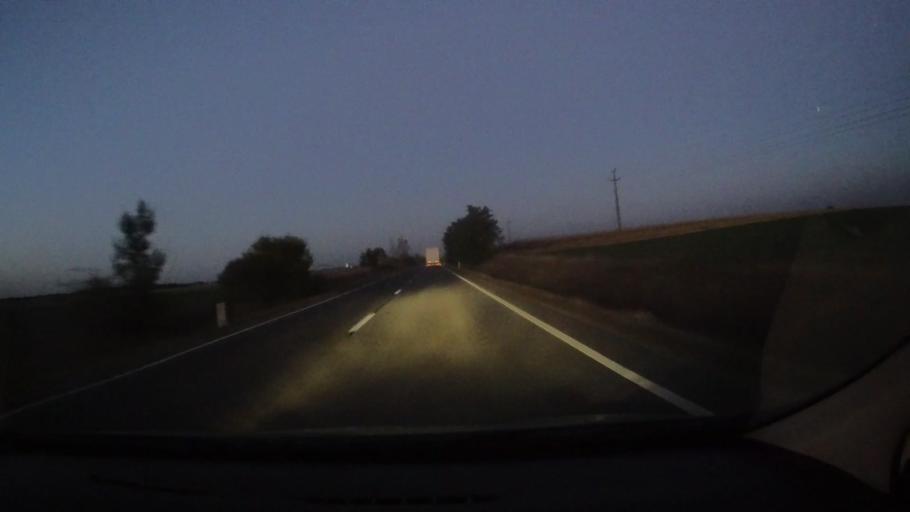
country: RO
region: Bihor
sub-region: Comuna Curtuiuseni
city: Curtuiseni
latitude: 47.5251
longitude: 22.1829
